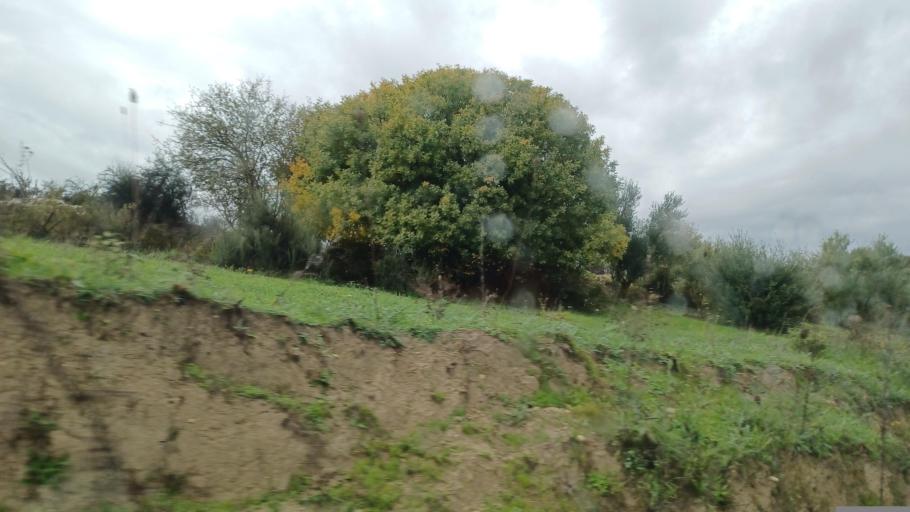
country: CY
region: Pafos
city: Mesogi
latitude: 34.8616
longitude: 32.5379
